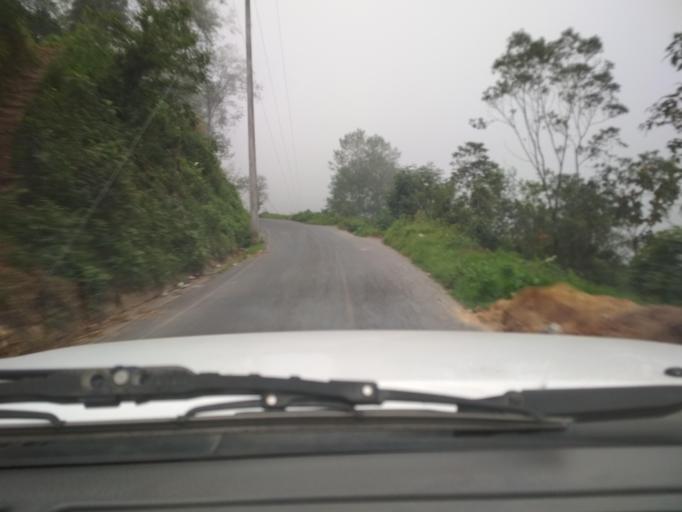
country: MX
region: Veracruz
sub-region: La Perla
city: Metlac Hernandez (Metlac Primero)
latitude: 18.9695
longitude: -97.1467
